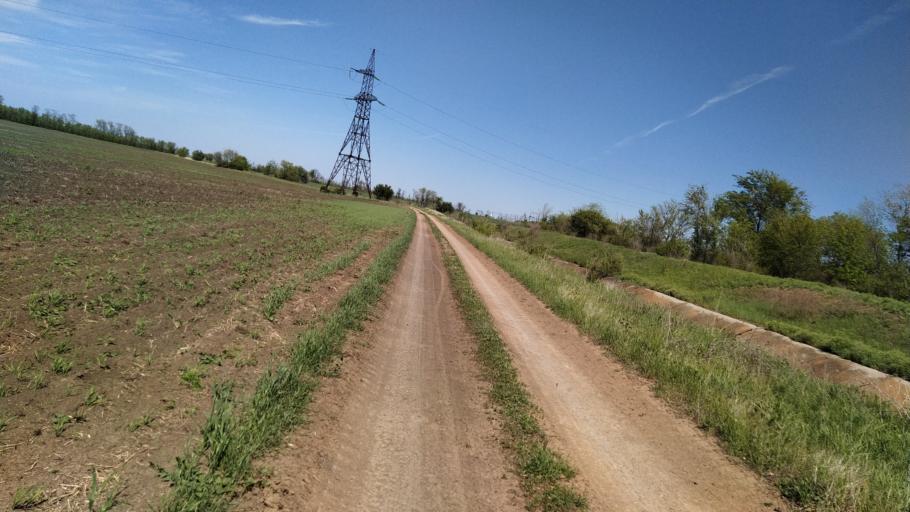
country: RU
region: Rostov
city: Kuleshovka
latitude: 47.0393
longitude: 39.6423
